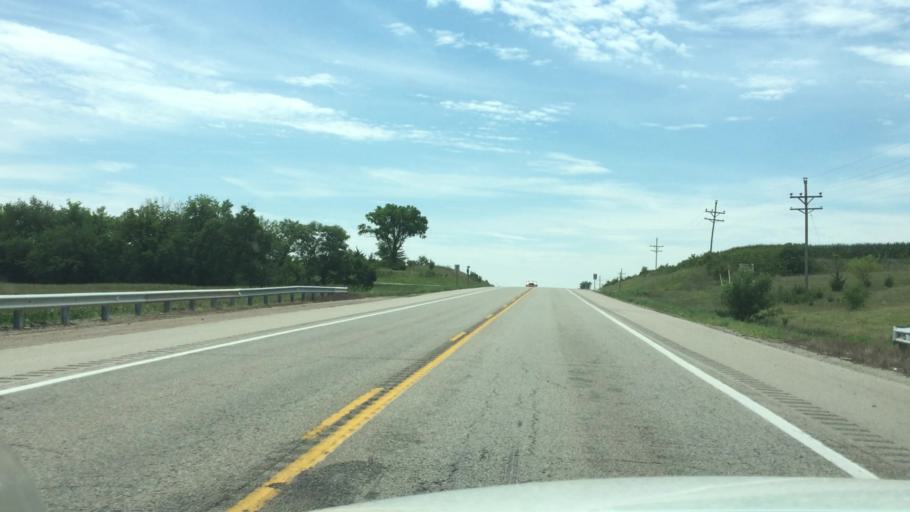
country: US
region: Kansas
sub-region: Nemaha County
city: Sabetha
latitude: 39.7988
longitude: -95.7294
